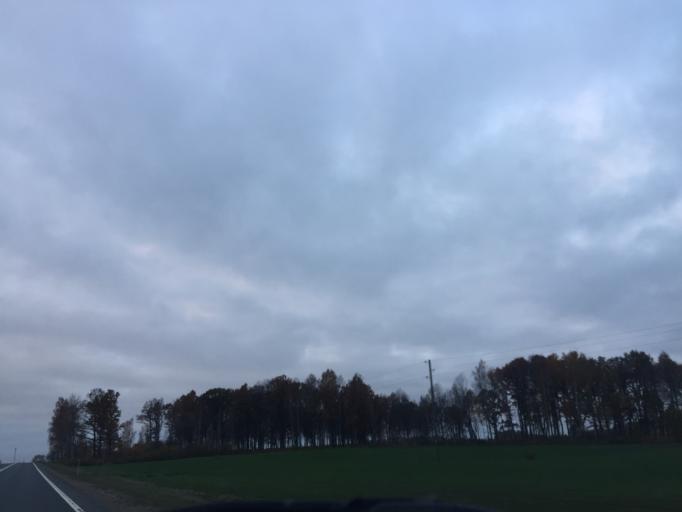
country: LV
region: Durbe
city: Liegi
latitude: 56.5884
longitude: 21.4321
